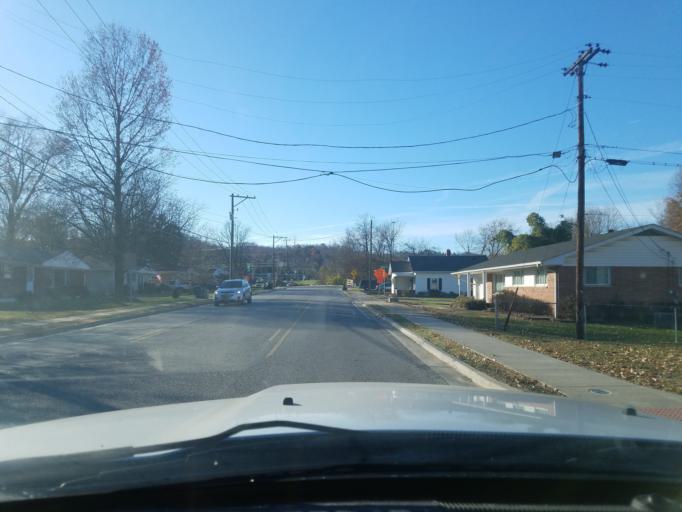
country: US
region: Indiana
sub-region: Floyd County
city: New Albany
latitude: 38.3101
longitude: -85.8408
